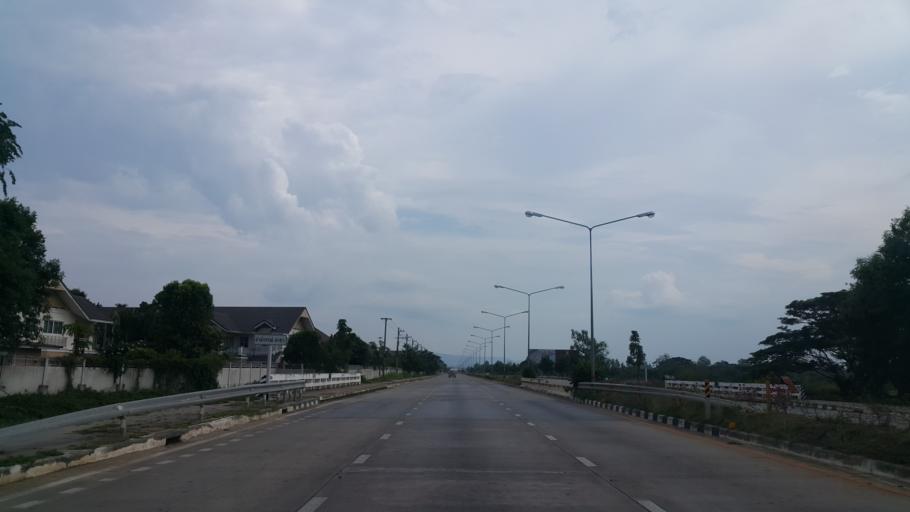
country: TH
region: Chiang Rai
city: Chiang Rai
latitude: 19.9058
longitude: 99.8595
